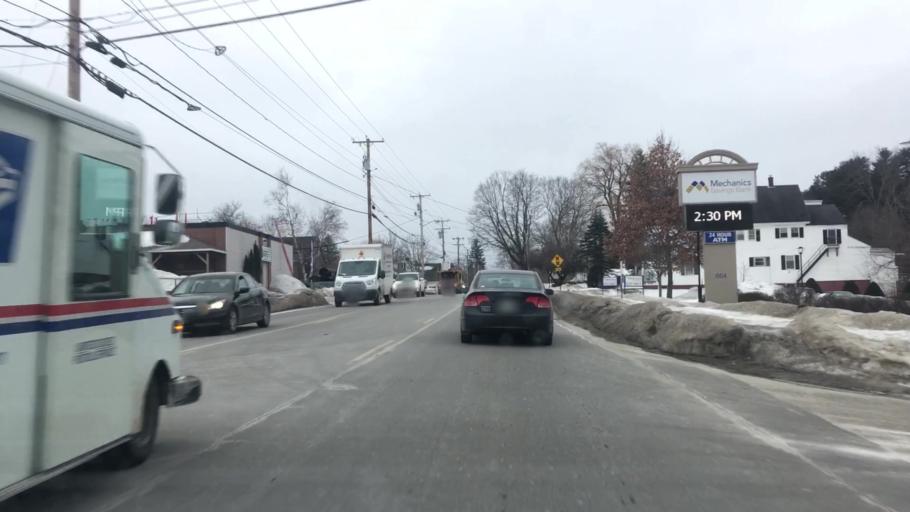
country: US
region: Maine
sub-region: Androscoggin County
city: Lewiston
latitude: 44.1198
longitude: -70.2037
